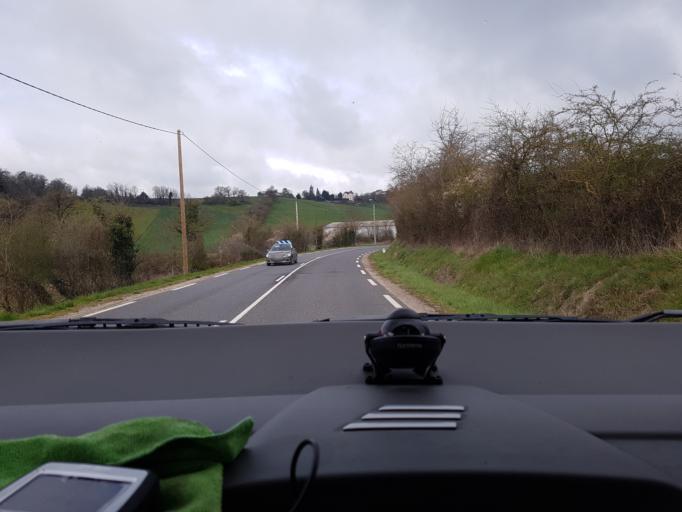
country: FR
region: Midi-Pyrenees
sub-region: Departement de l'Aveyron
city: Olemps
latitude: 44.3659
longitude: 2.5431
